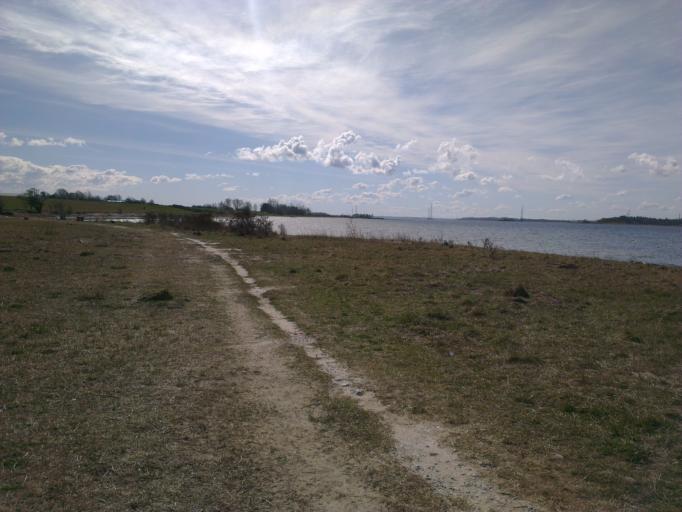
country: DK
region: Capital Region
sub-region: Frederikssund Kommune
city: Frederikssund
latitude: 55.8169
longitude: 12.0663
